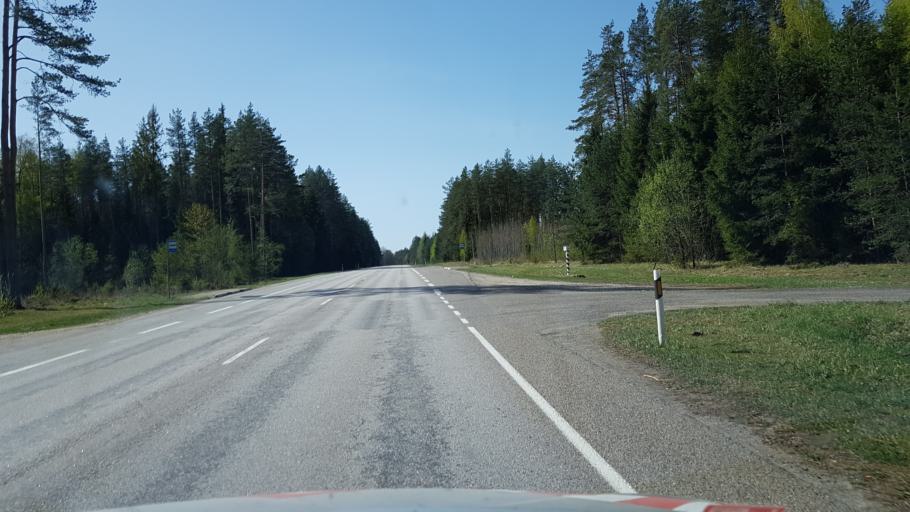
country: EE
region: Valgamaa
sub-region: Valga linn
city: Valga
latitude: 57.8231
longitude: 26.0512
